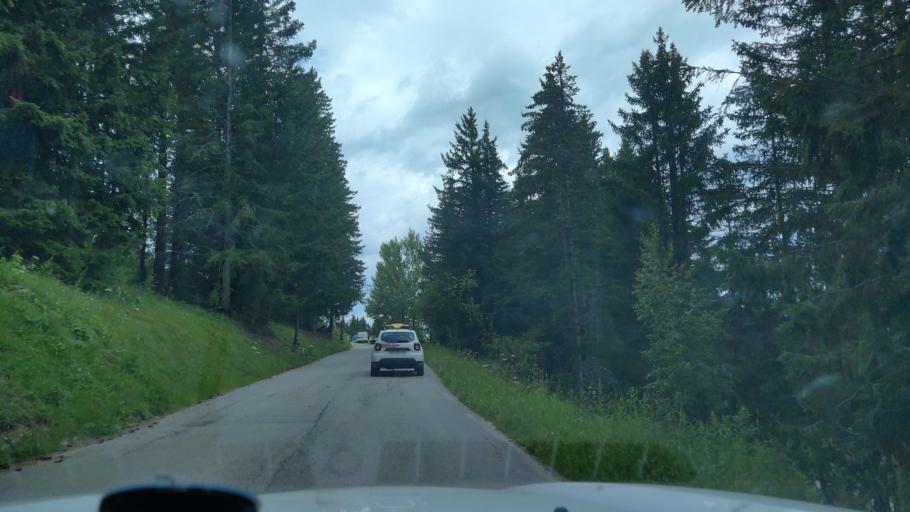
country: FR
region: Rhone-Alpes
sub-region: Departement de la Savoie
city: Courchevel
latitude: 45.4105
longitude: 6.6592
